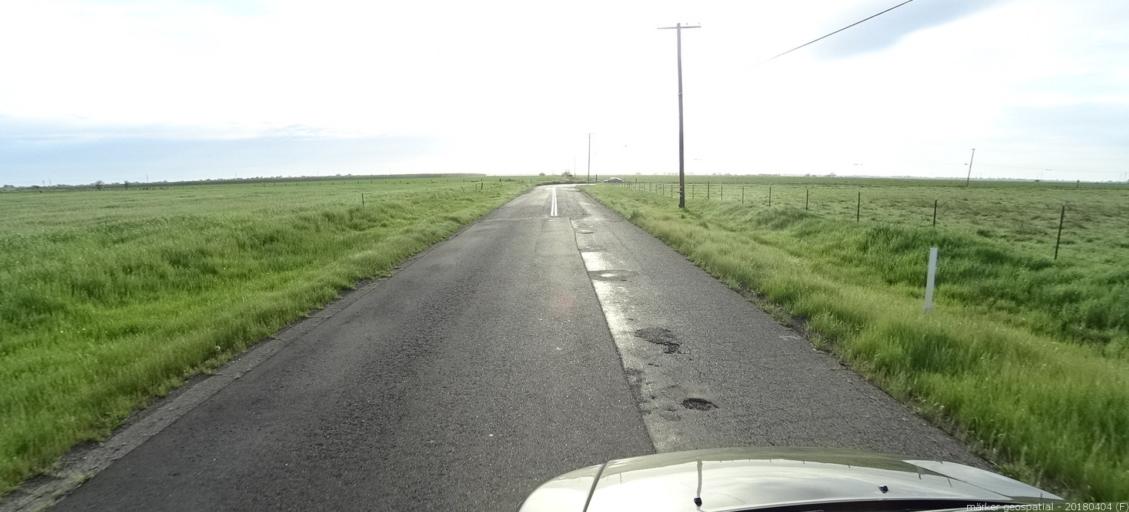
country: US
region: California
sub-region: Sacramento County
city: Wilton
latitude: 38.3713
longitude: -121.2991
